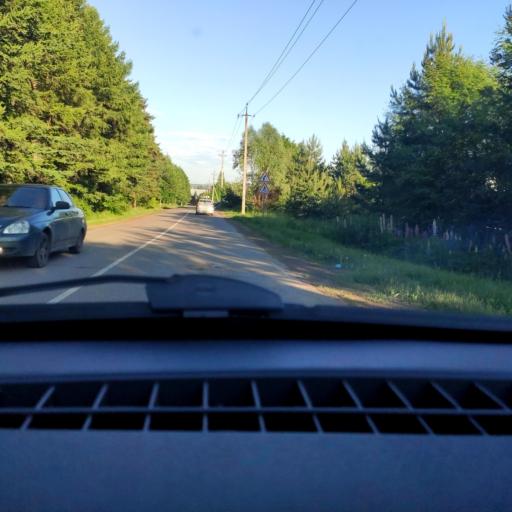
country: RU
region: Bashkortostan
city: Avdon
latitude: 54.6463
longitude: 55.7045
